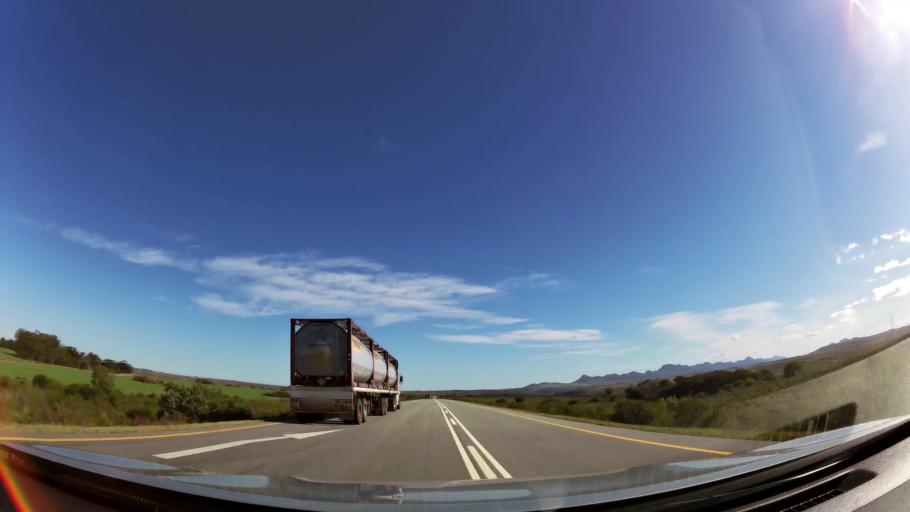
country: ZA
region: Eastern Cape
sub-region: Cacadu District Municipality
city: Kruisfontein
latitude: -34.0210
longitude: 24.6163
